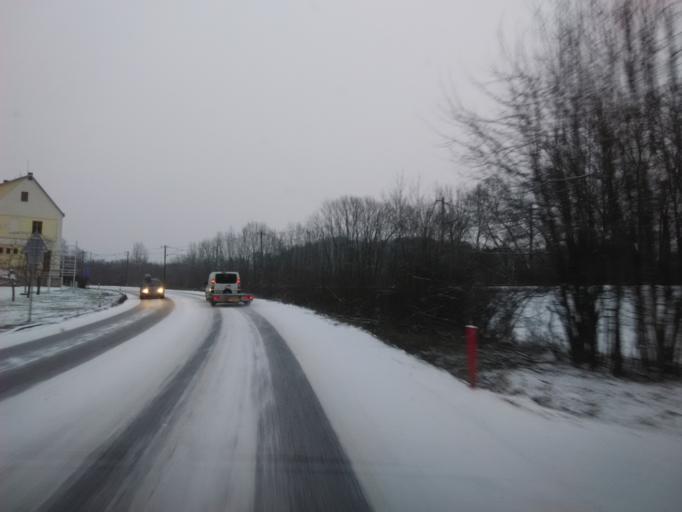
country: CZ
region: Olomoucky
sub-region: Okres Prerov
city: Hranice
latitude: 49.5275
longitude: 17.7507
